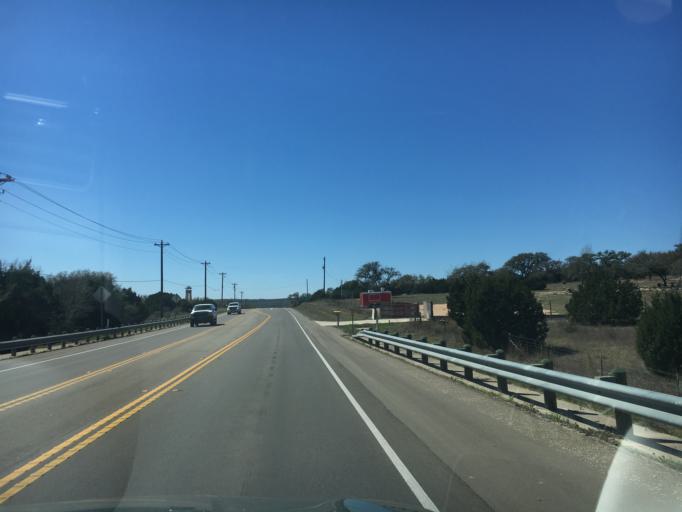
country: US
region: Texas
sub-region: Travis County
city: The Hills
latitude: 30.2921
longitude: -98.0317
